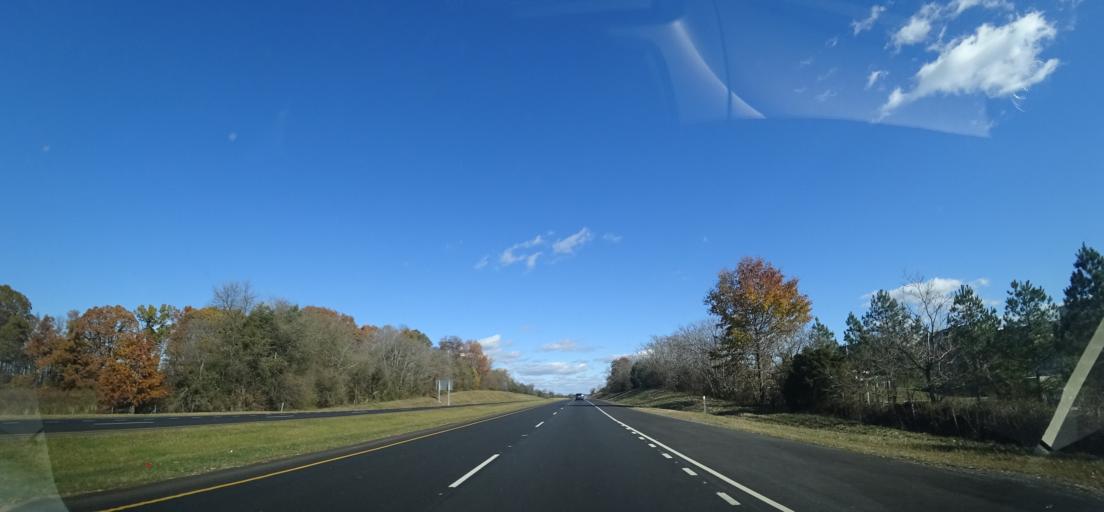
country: US
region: Virginia
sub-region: Culpeper County
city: Culpeper
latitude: 38.4773
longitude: -77.9477
